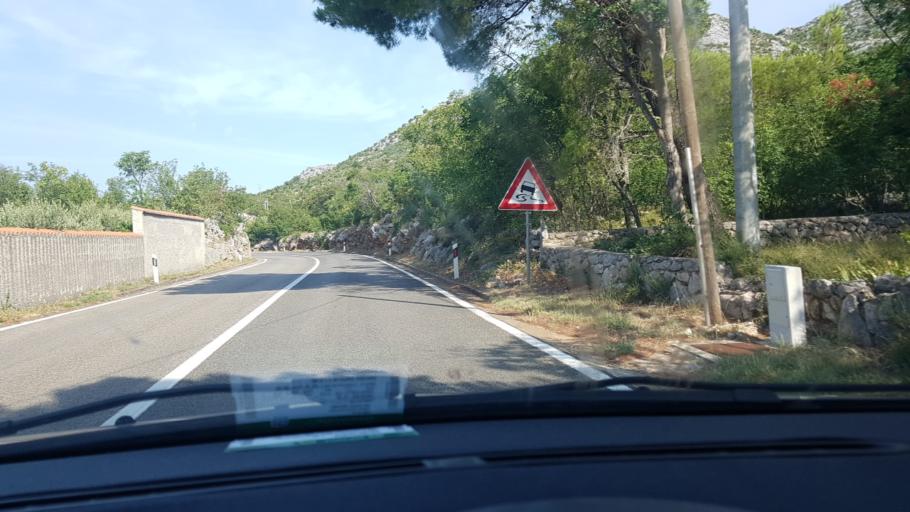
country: HR
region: Zadarska
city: Starigrad
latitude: 44.3187
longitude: 15.4095
